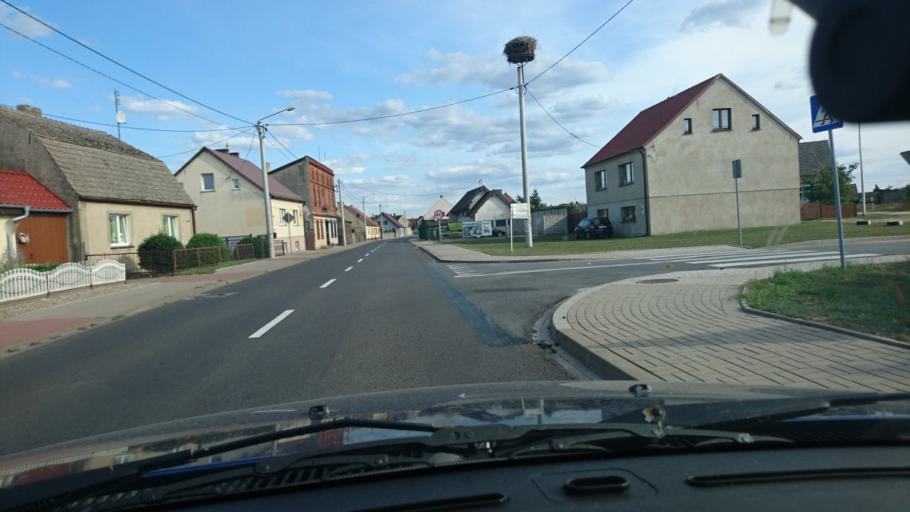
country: PL
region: Greater Poland Voivodeship
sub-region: Powiat krotoszynski
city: Sulmierzyce
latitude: 51.6120
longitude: 17.5166
